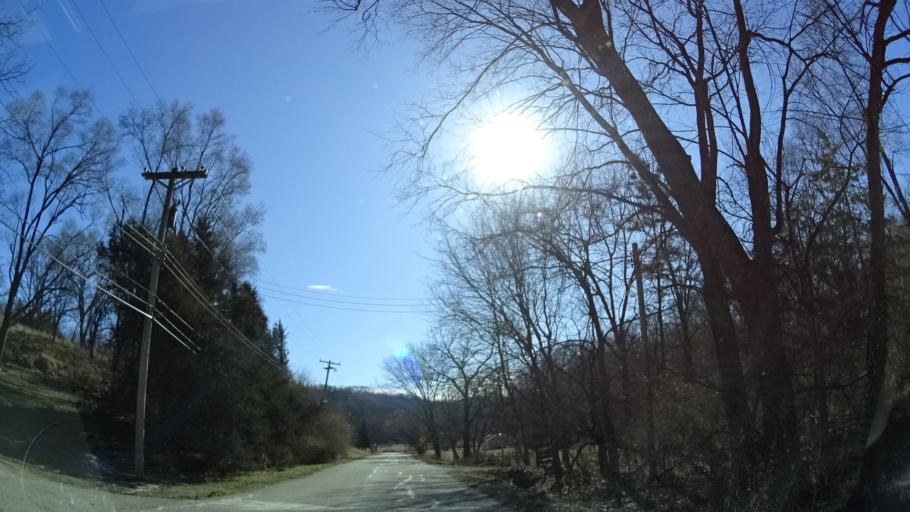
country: US
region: Nebraska
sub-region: Sarpy County
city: Bellevue
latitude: 41.1564
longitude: -95.8951
